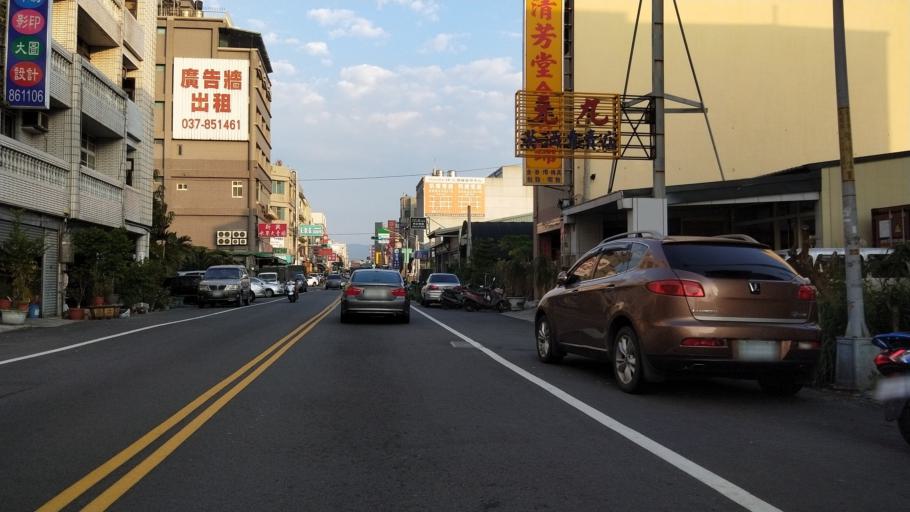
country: TW
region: Taiwan
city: Fengyuan
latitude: 24.4410
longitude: 120.6515
